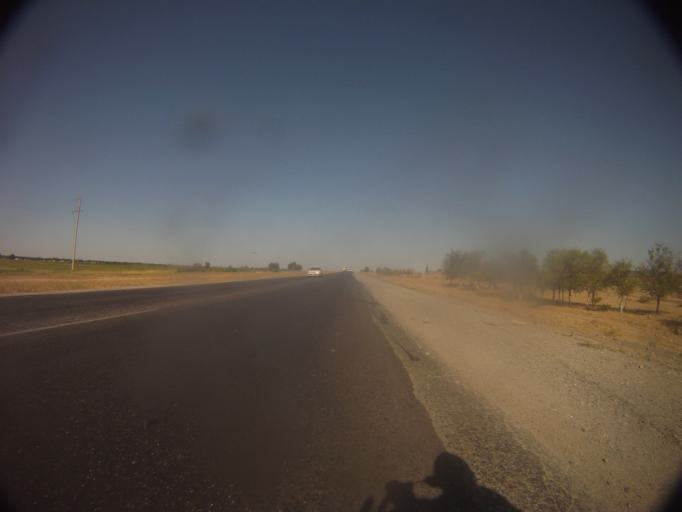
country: KZ
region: Zhambyl
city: Sarykemer
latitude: 42.9237
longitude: 71.4828
